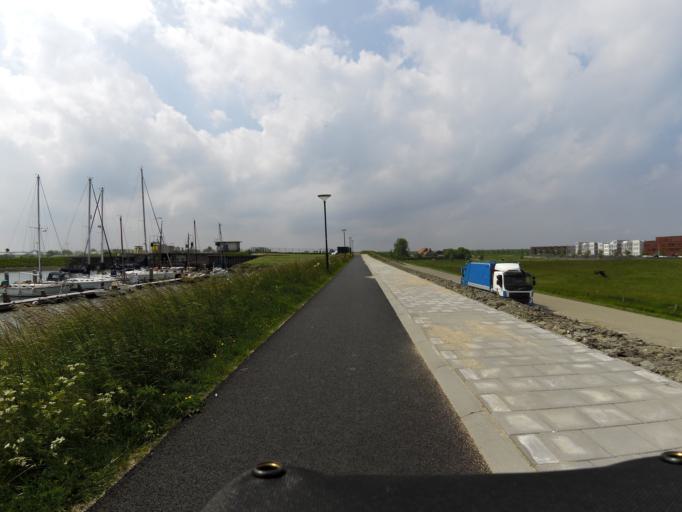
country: NL
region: Zeeland
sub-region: Schouwen-Duiveland
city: Scharendijke
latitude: 51.6435
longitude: 3.9118
